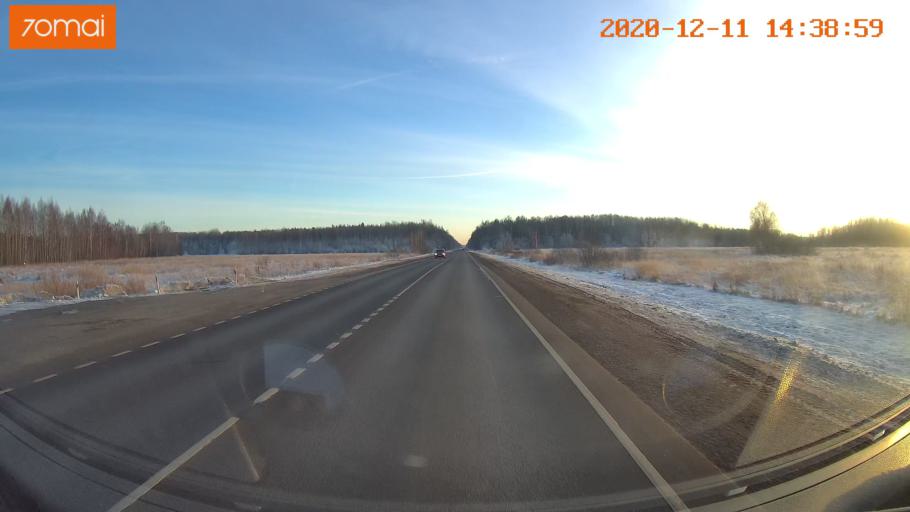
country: RU
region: Kostroma
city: Volgorechensk
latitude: 57.5325
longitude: 41.0200
